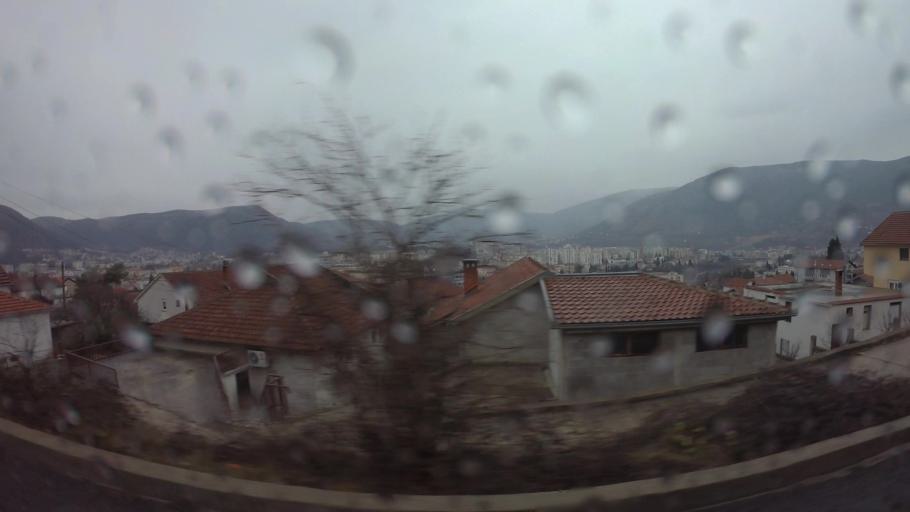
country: BA
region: Federation of Bosnia and Herzegovina
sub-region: Hercegovacko-Bosanski Kanton
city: Mostar
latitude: 43.3485
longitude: 17.8167
